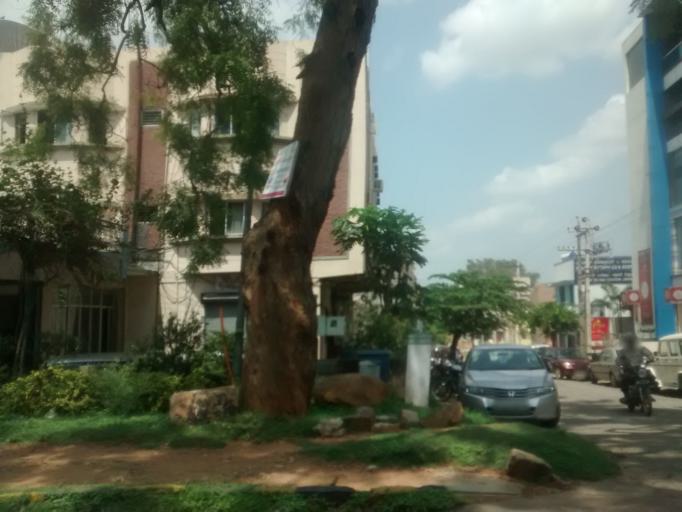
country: IN
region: Karnataka
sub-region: Mysore
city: Mysore
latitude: 12.3047
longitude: 76.6436
